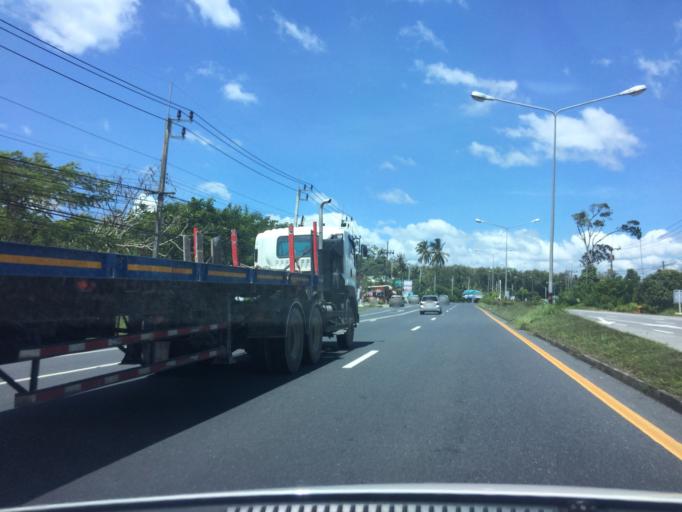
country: TH
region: Phangnga
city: Thai Mueang
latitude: 8.2348
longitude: 98.2971
